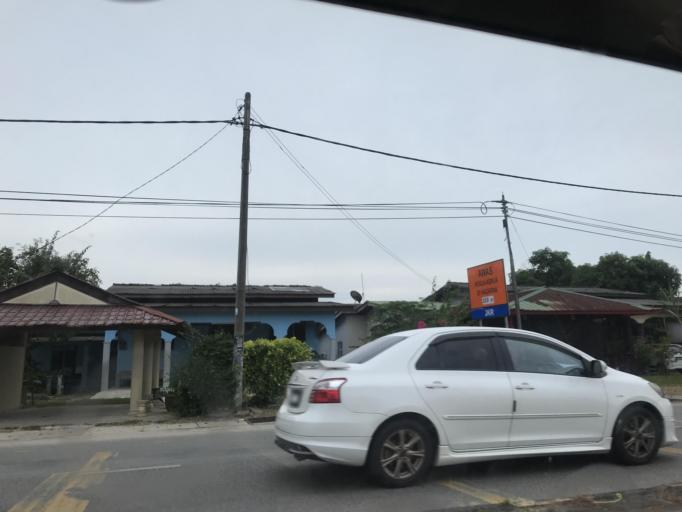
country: MY
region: Kelantan
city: Kota Bharu
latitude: 6.1201
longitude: 102.2101
